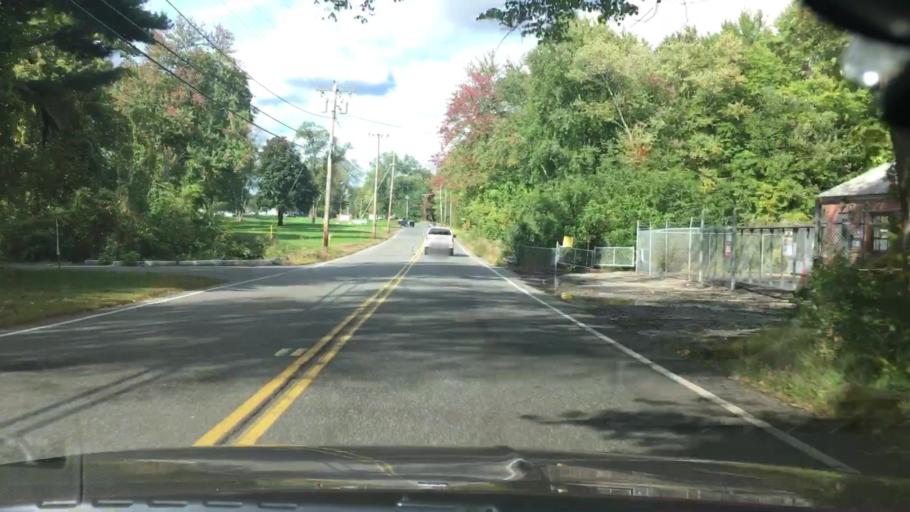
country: US
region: Massachusetts
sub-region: Hampden County
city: East Longmeadow
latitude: 42.0400
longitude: -72.5177
